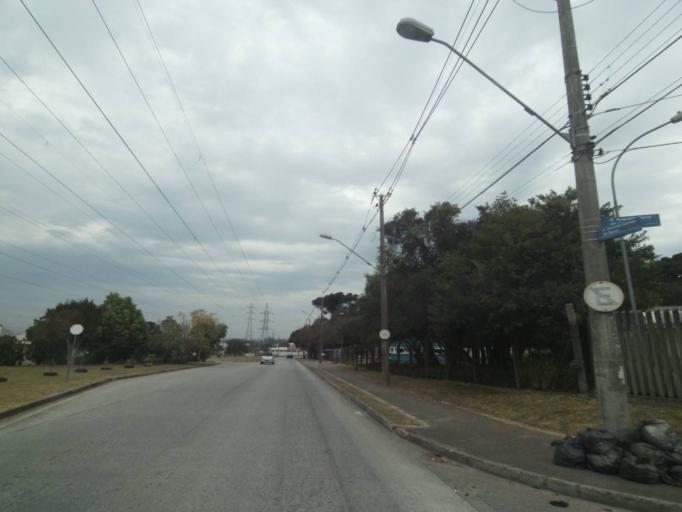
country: BR
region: Parana
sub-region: Sao Jose Dos Pinhais
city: Sao Jose dos Pinhais
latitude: -25.4886
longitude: -49.2071
